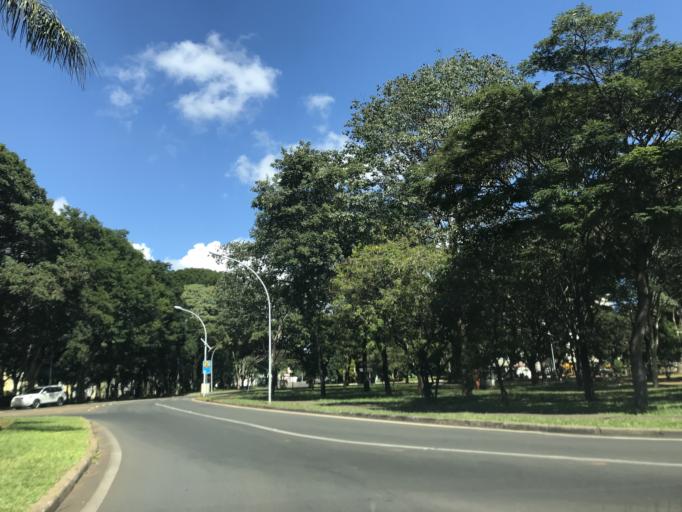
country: BR
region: Federal District
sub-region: Brasilia
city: Brasilia
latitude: -15.8238
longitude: -47.9045
